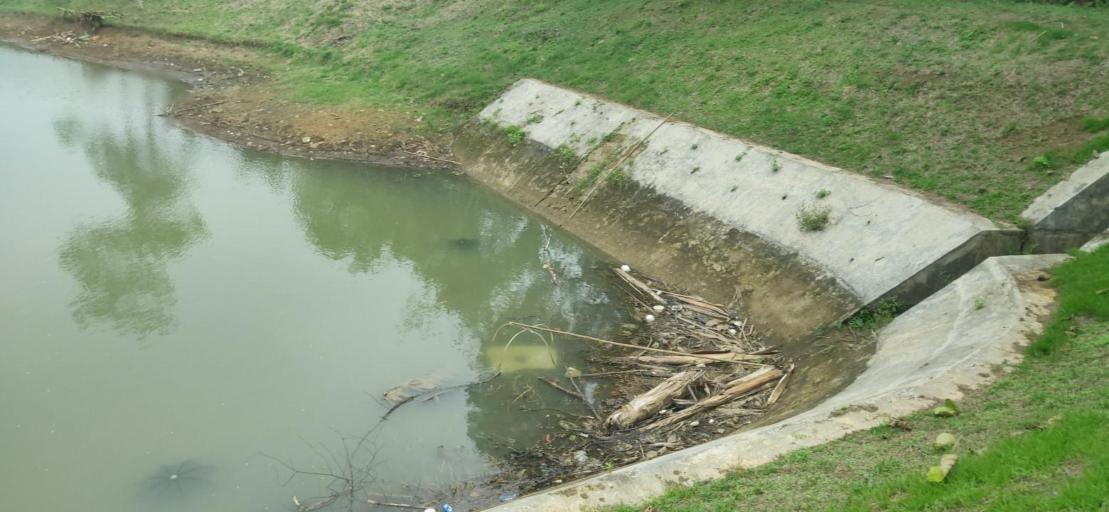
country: ID
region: West Java
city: Garisul
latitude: -6.4715
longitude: 106.4936
